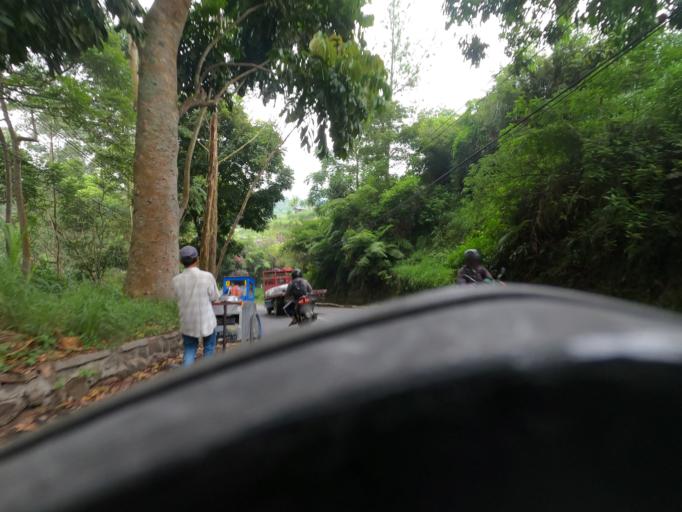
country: ID
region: West Java
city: Lembang
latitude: -6.7981
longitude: 107.5787
